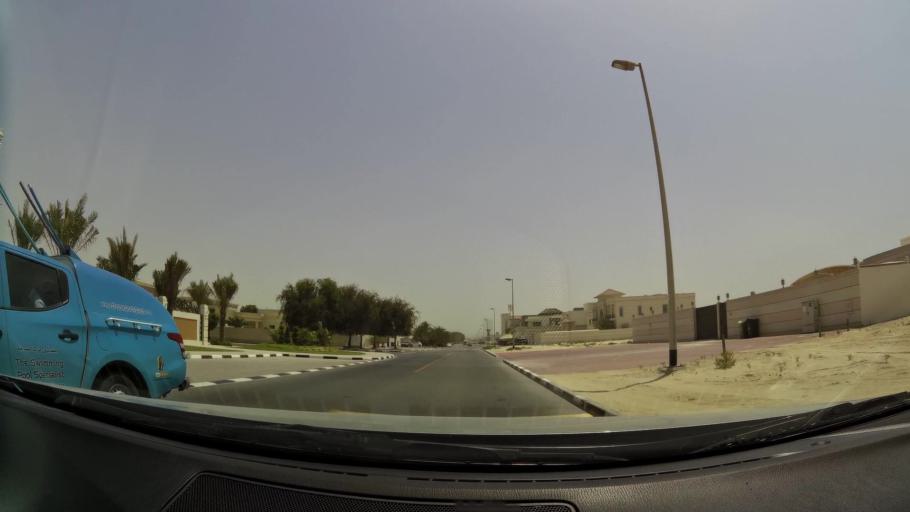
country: AE
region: Dubai
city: Dubai
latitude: 25.1353
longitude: 55.2080
